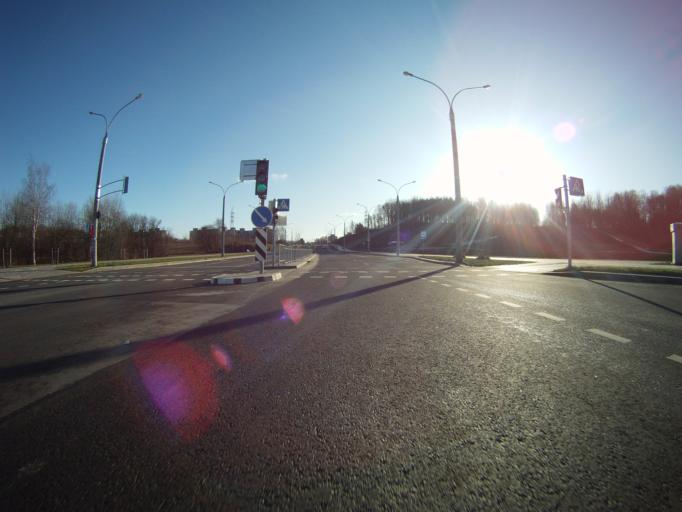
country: BY
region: Minsk
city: Novoye Medvezhino
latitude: 53.8734
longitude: 27.4561
